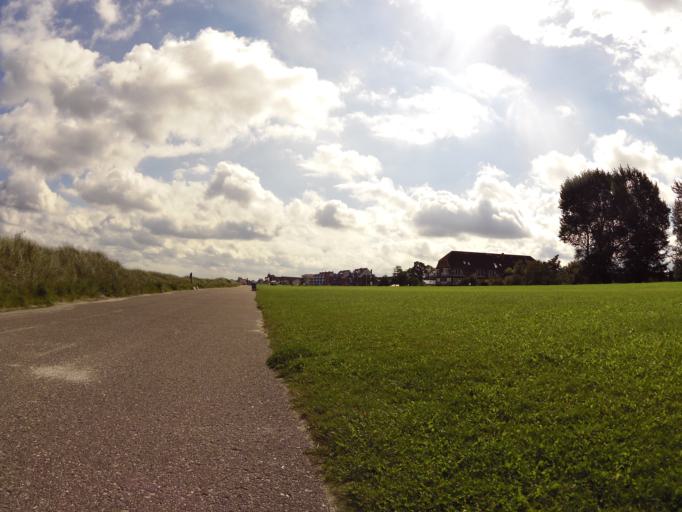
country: DE
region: Schleswig-Holstein
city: Krummbek
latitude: 54.4172
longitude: 10.4091
